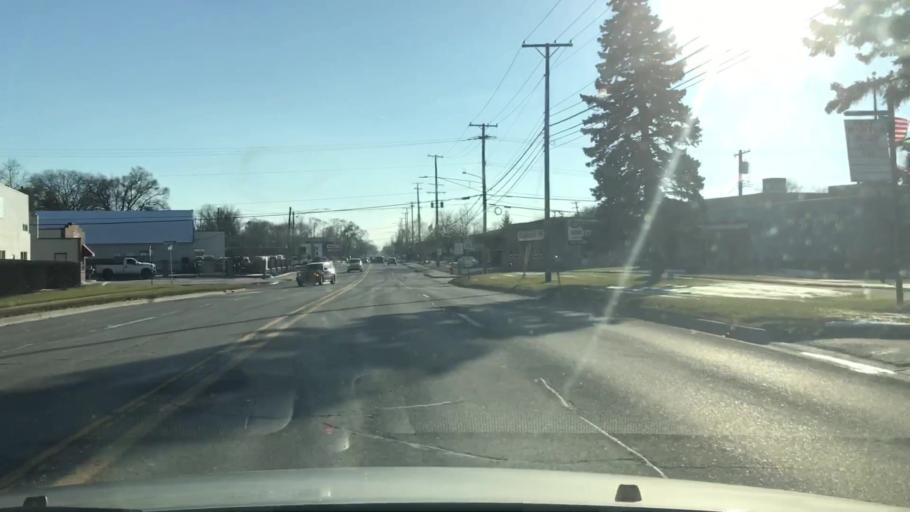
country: US
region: Michigan
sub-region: Oakland County
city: Clawson
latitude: 42.5416
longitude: -83.1340
